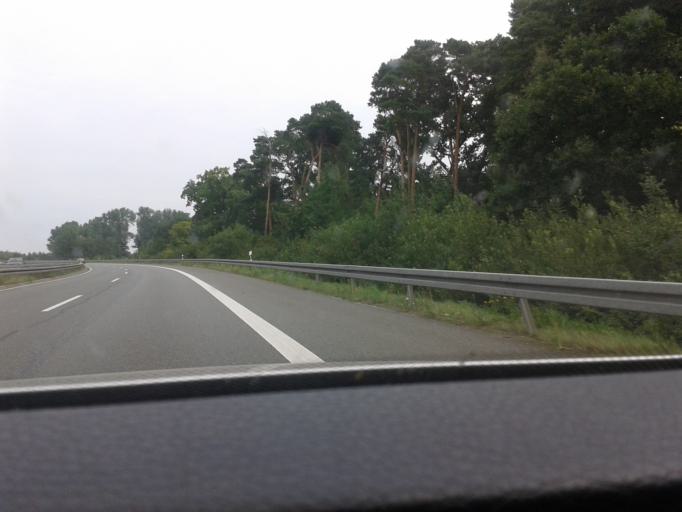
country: DE
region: Lower Saxony
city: Tappenbeck
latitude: 52.4474
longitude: 10.7368
